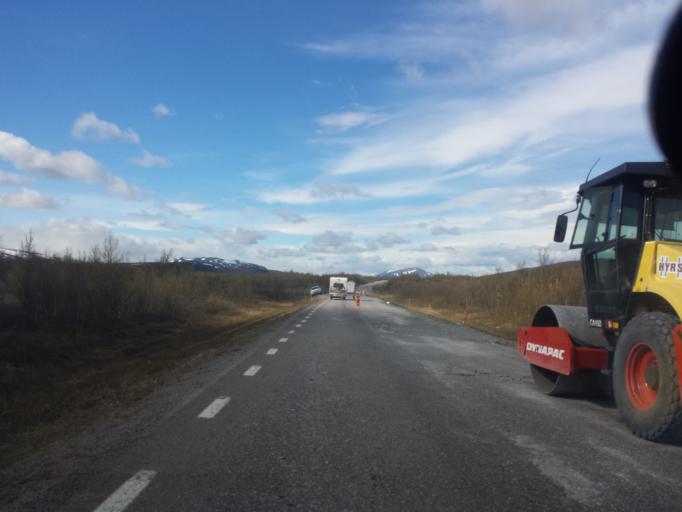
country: SE
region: Norrbotten
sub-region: Kiruna Kommun
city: Kiruna
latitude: 68.0126
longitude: 19.8423
